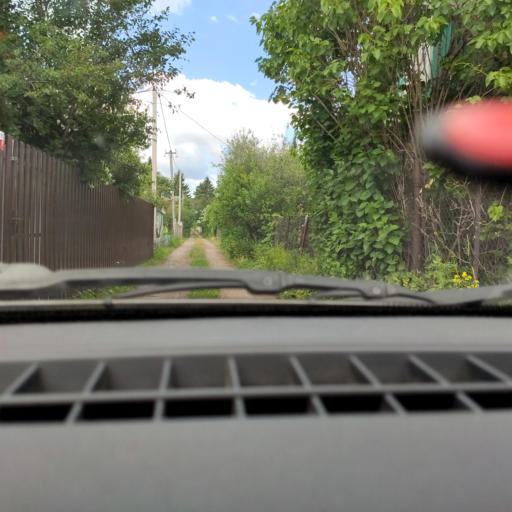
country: RU
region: Bashkortostan
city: Ufa
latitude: 54.6390
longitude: 55.9179
